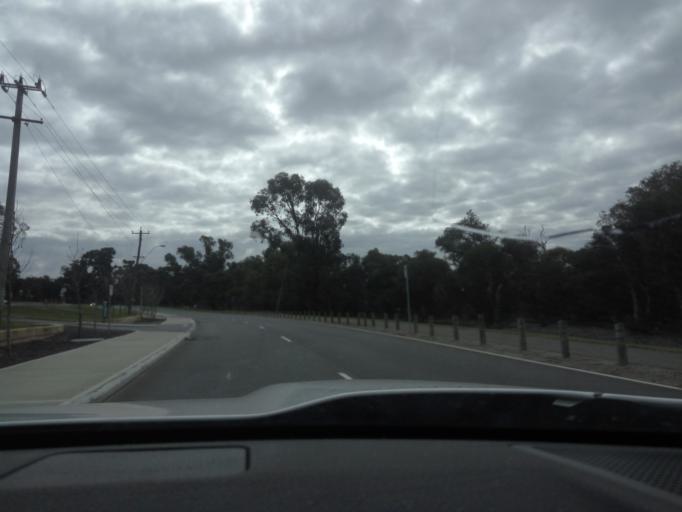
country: AU
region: Western Australia
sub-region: City of Cockburn
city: Bibra Lake
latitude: -32.0935
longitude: 115.8204
